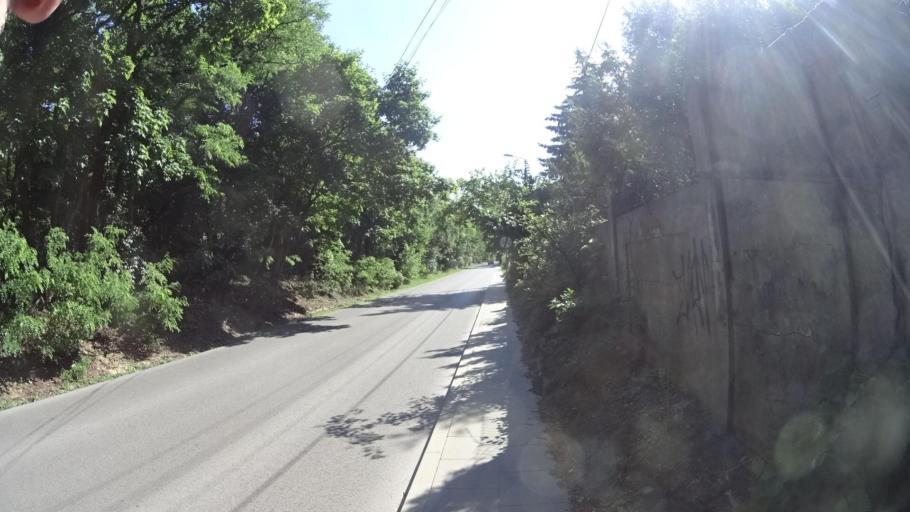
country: PL
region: Masovian Voivodeship
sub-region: Warszawa
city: Bialoleka
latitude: 52.3370
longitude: 20.9783
